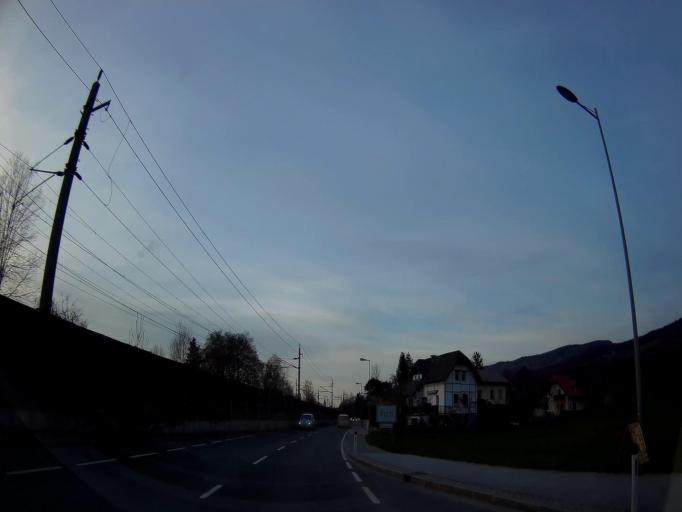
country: AT
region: Salzburg
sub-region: Politischer Bezirk Hallein
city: Puch bei Hallein
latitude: 47.7072
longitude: 13.0927
